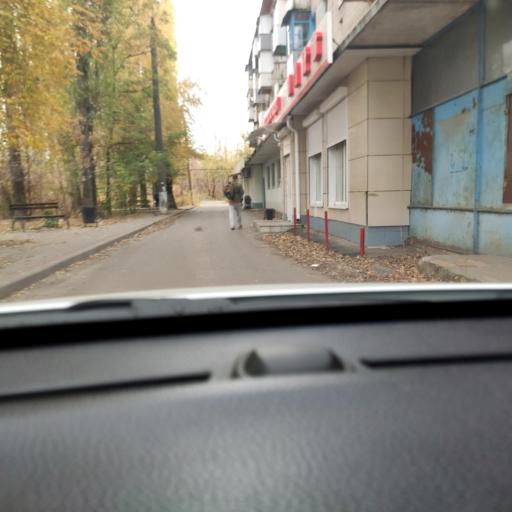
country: RU
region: Voronezj
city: Novaya Usman'
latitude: 51.6481
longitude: 39.3024
